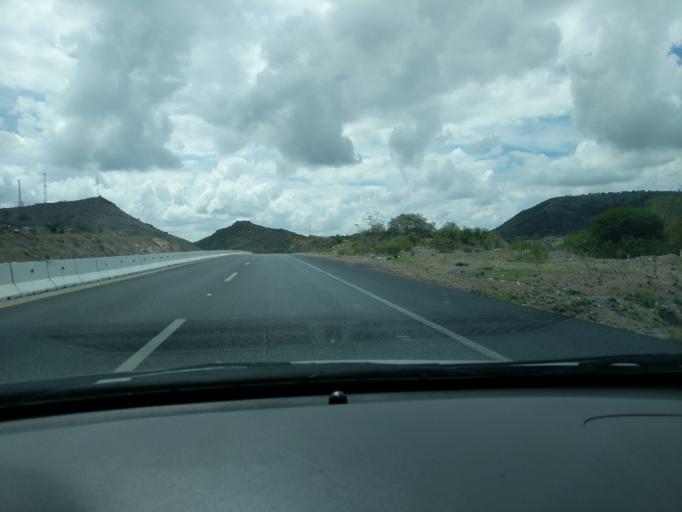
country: MX
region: San Luis Potosi
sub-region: Mexquitic de Carmona
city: Cerrito de Jaral
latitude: 22.2530
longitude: -101.1150
